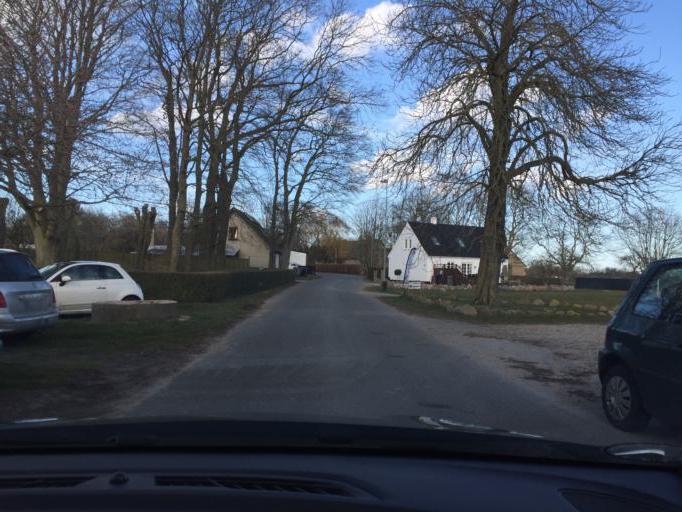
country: DK
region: South Denmark
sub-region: Nyborg Kommune
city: Ullerslev
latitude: 55.3519
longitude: 10.7207
